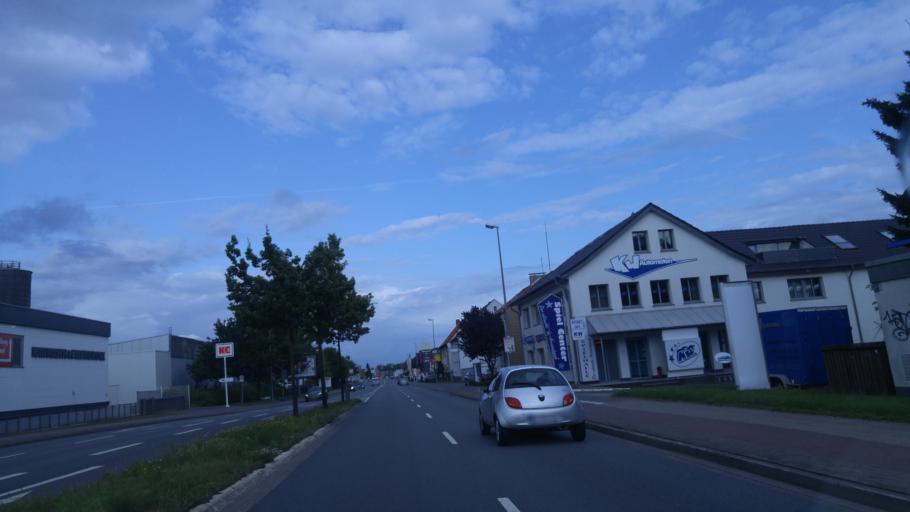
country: DE
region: North Rhine-Westphalia
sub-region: Regierungsbezirk Detmold
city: Bielefeld
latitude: 52.0342
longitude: 8.5618
